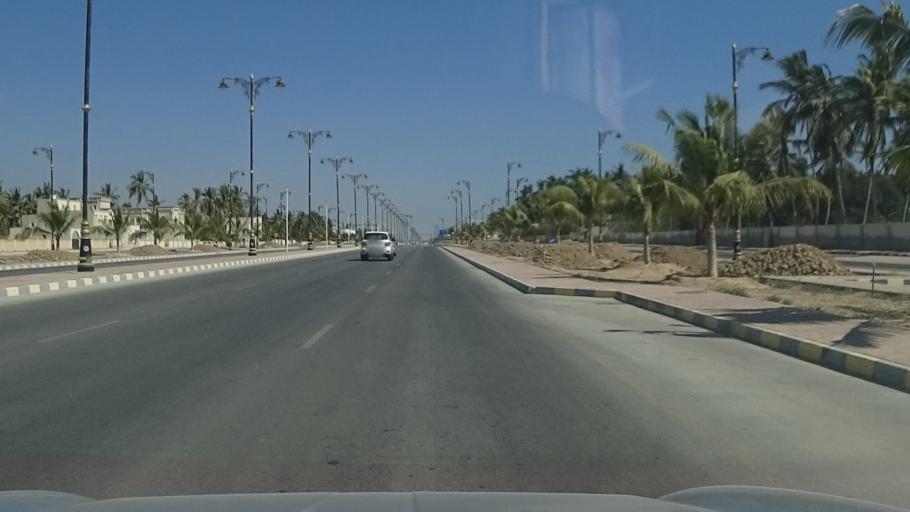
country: OM
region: Zufar
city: Salalah
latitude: 17.0363
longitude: 54.1545
